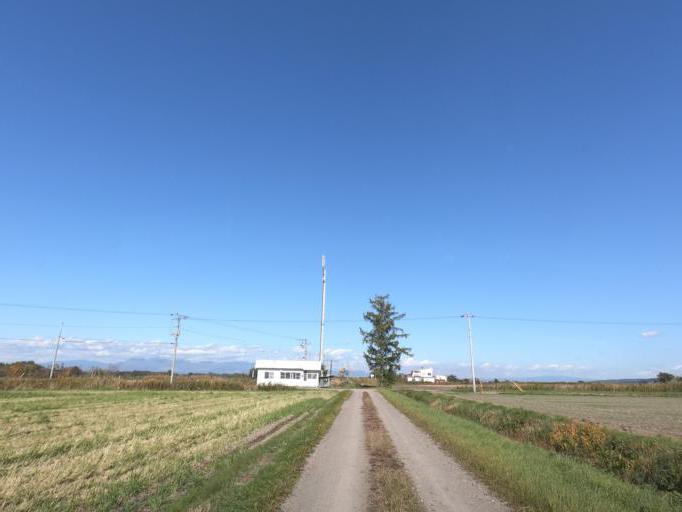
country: JP
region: Hokkaido
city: Otofuke
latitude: 43.0369
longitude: 143.2724
